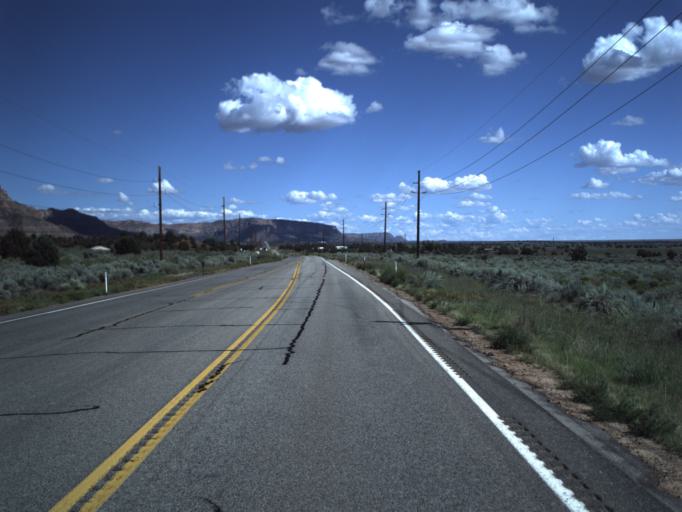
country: US
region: Arizona
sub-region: Mohave County
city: Colorado City
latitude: 37.0431
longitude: -113.0818
